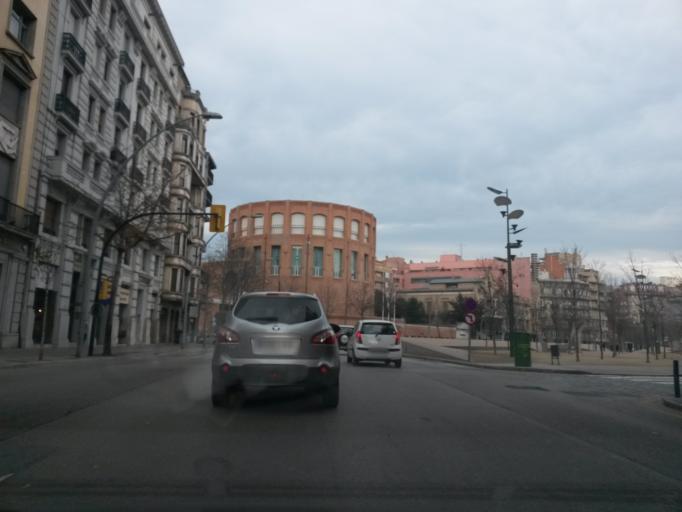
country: ES
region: Catalonia
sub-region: Provincia de Girona
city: Girona
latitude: 41.9830
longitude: 2.8198
